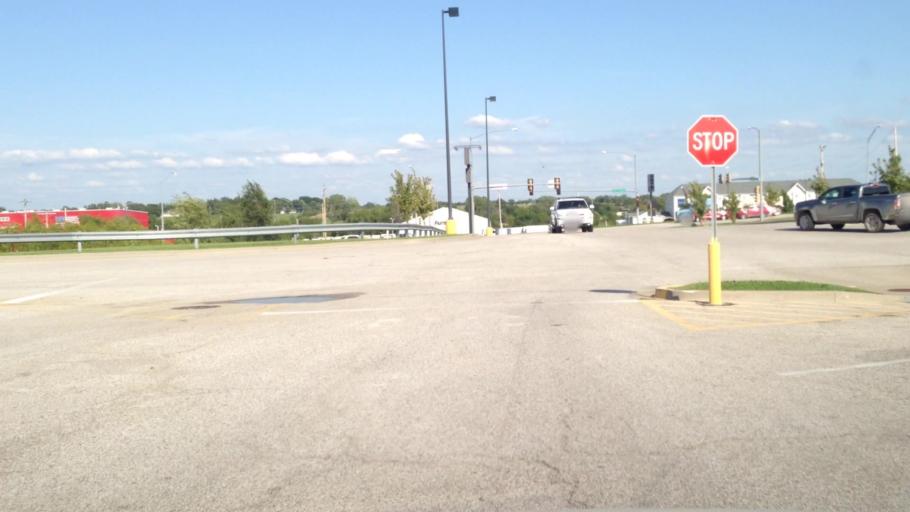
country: US
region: Kansas
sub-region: Bourbon County
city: Fort Scott
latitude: 37.8084
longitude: -94.7069
